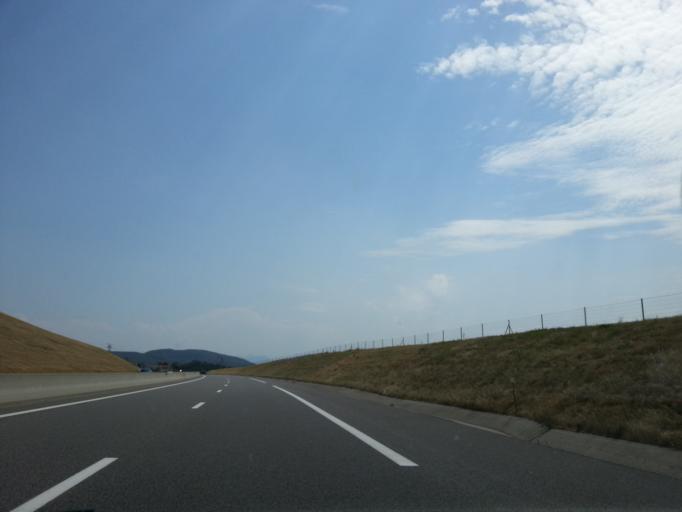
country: FR
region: Rhone-Alpes
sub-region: Departement de la Haute-Savoie
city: Cruseilles
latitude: 46.0480
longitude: 6.0812
